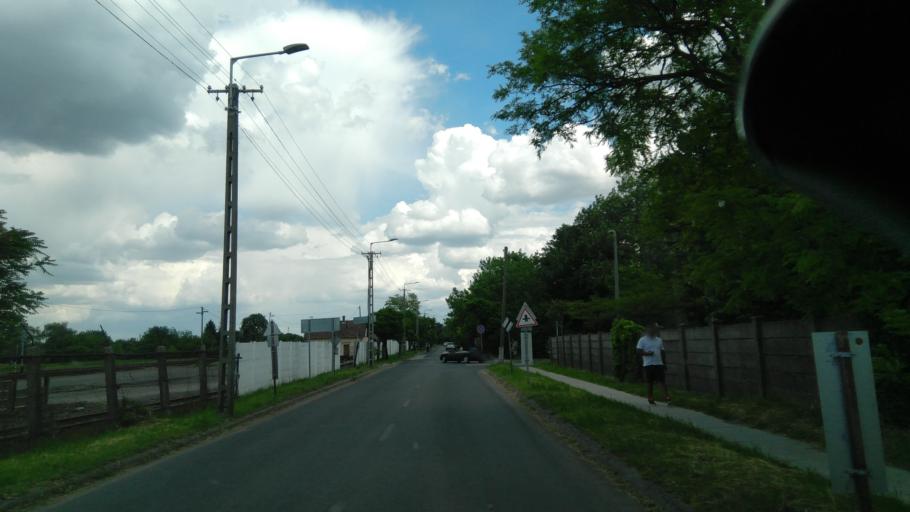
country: HU
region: Bekes
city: Gyula
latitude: 46.6562
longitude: 21.2695
